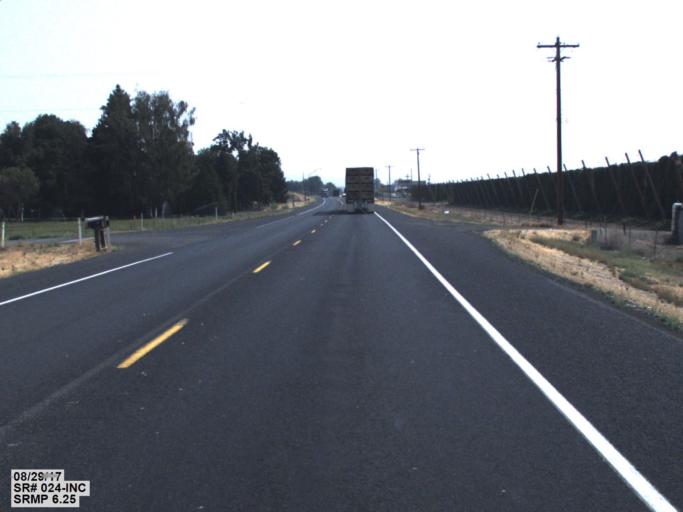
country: US
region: Washington
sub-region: Yakima County
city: Terrace Heights
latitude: 46.5495
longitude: -120.3618
